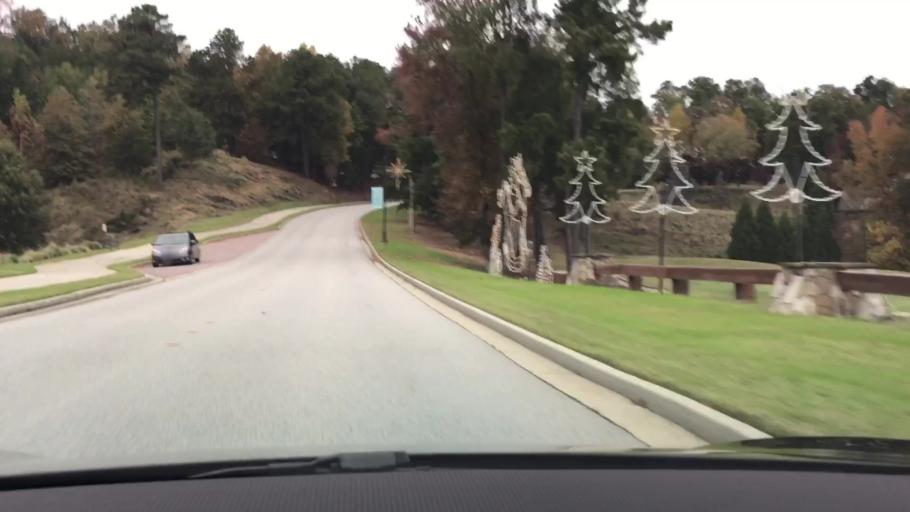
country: US
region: Georgia
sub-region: Gwinnett County
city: Buford
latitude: 34.1835
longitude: -84.0187
